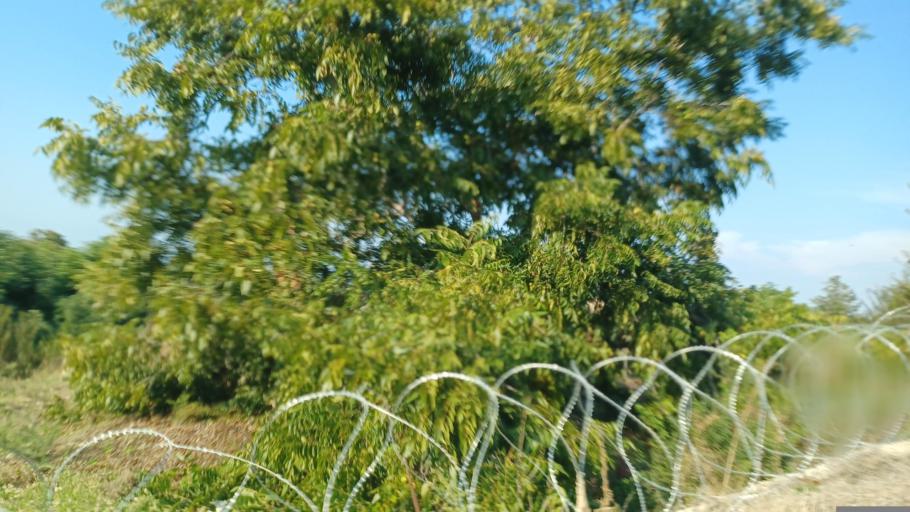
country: CY
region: Pafos
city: Kissonerga
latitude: 34.8381
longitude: 32.3957
